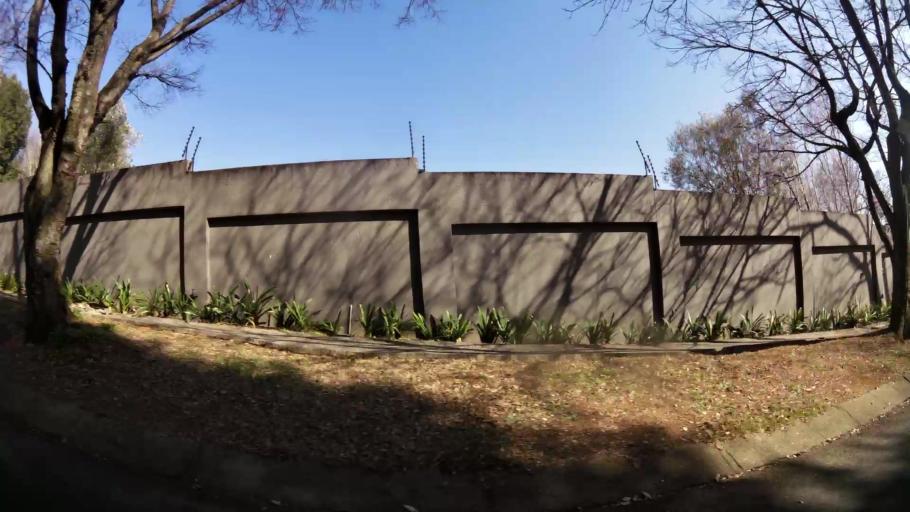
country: ZA
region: Gauteng
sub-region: City of Johannesburg Metropolitan Municipality
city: Modderfontein
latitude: -26.1397
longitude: 28.1023
